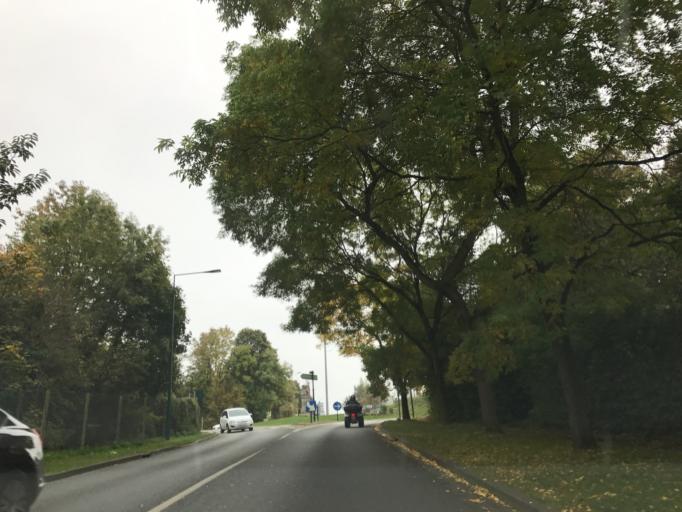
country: FR
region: Nord-Pas-de-Calais
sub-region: Departement du Pas-de-Calais
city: Saint-Laurent-Blangy
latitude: 50.2962
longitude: 2.8041
